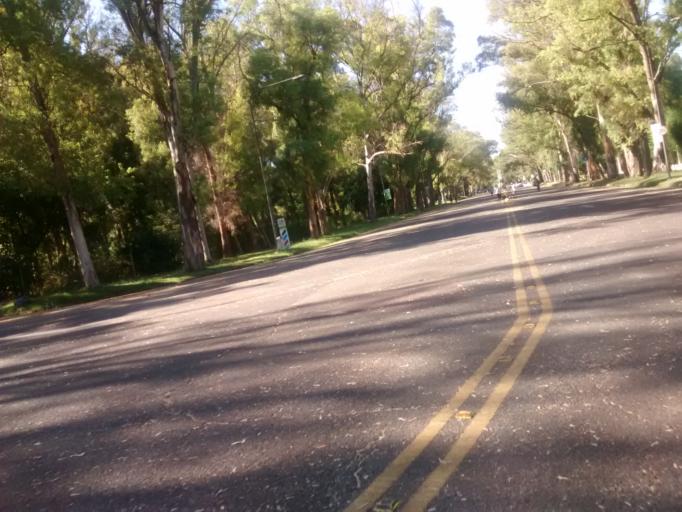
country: AR
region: Buenos Aires
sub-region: Partido de La Plata
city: La Plata
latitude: -34.9050
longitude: -57.9337
